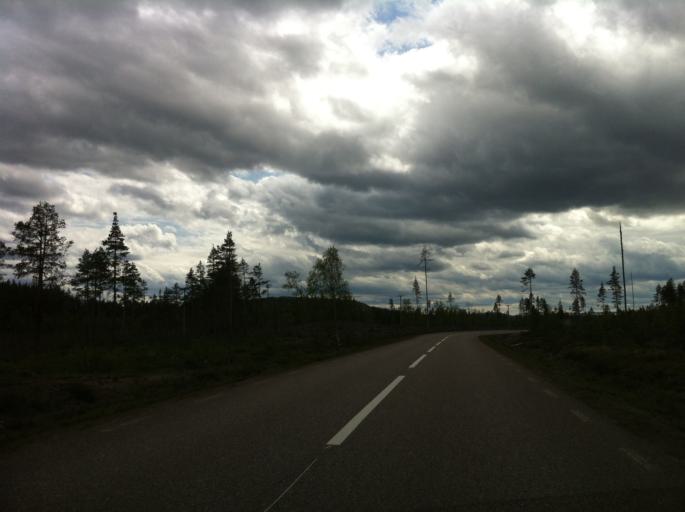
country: NO
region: Hedmark
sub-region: Trysil
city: Innbygda
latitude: 61.4333
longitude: 13.0961
